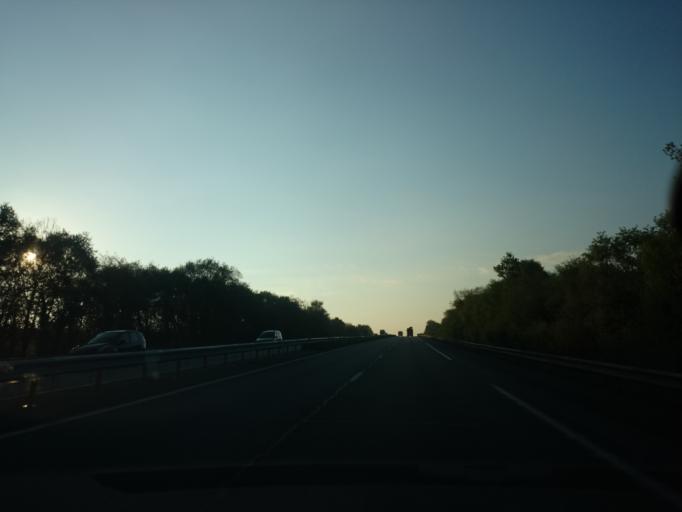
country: FR
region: Brittany
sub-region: Departement du Finistere
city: Chateaulin
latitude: 48.2314
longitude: -4.0977
